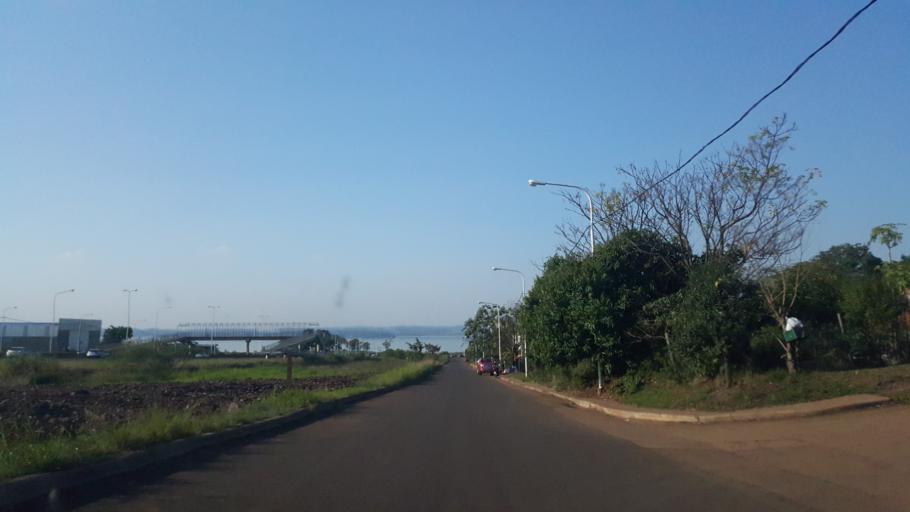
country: AR
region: Misiones
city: Garupa
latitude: -27.4503
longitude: -55.8543
